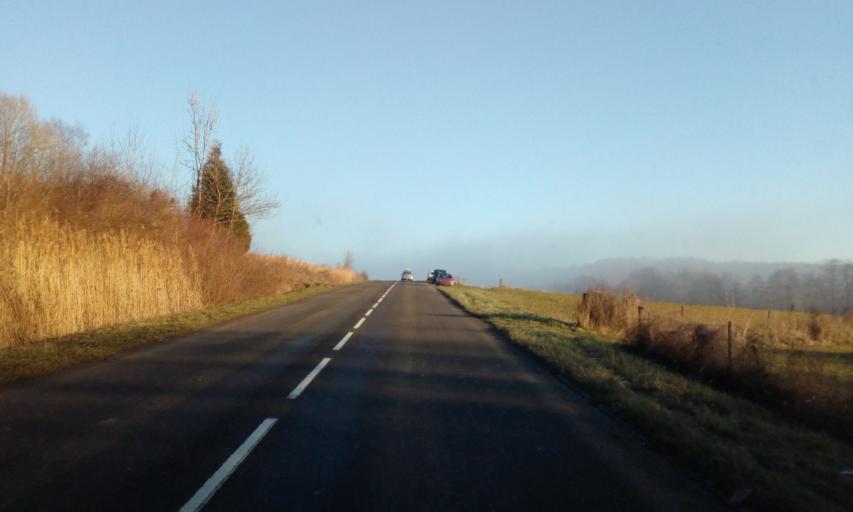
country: FR
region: Champagne-Ardenne
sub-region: Departement des Ardennes
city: Rimogne
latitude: 49.7756
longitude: 4.4206
